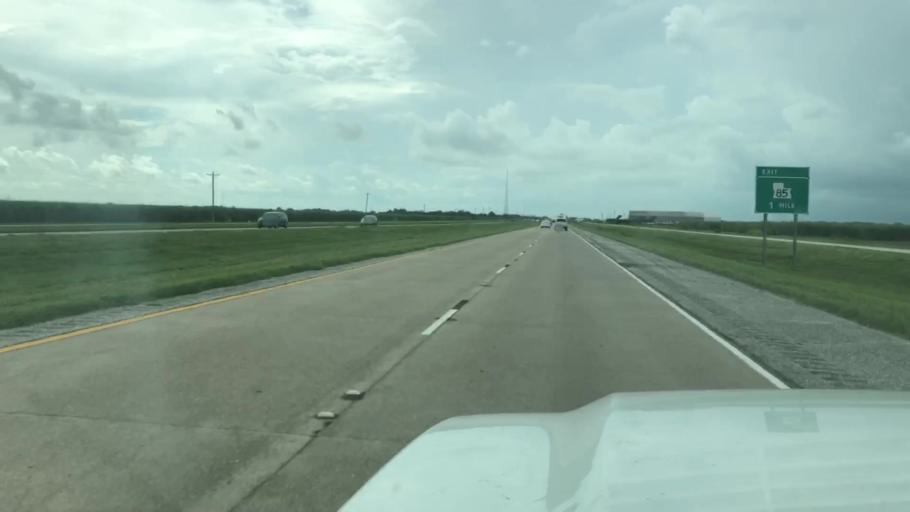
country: US
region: Louisiana
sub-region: Iberia Parish
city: Jeanerette
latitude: 29.9077
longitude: -91.7103
